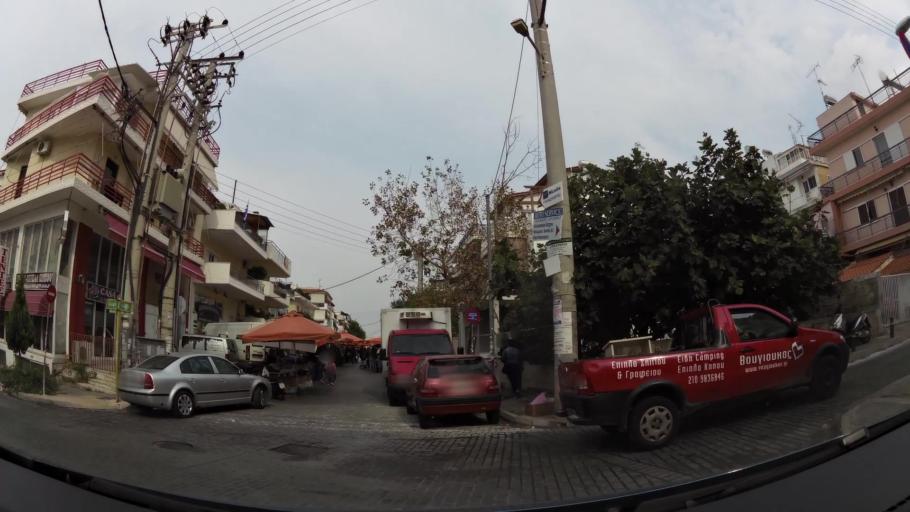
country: GR
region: Attica
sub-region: Nomarchia Athinas
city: Agios Dimitrios
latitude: 37.9276
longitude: 23.7295
